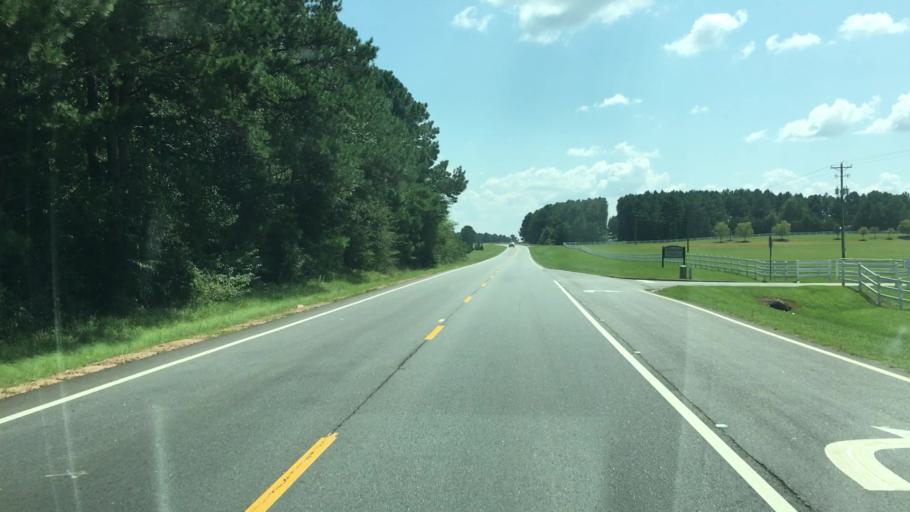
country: US
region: Georgia
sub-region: Oconee County
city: Watkinsville
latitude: 33.7589
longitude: -83.4348
